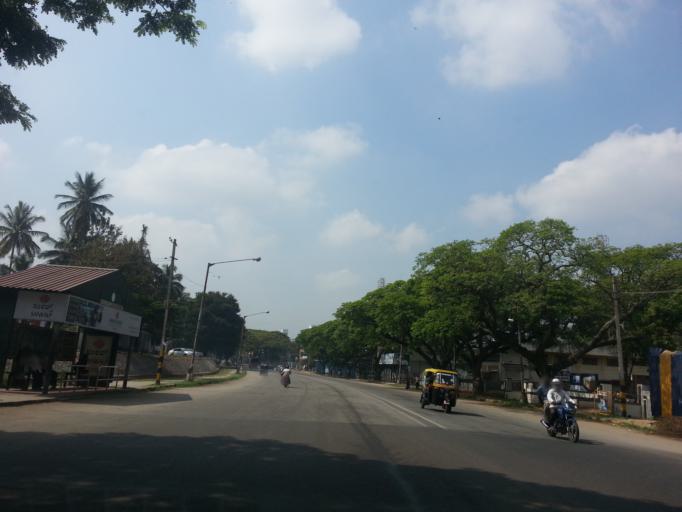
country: IN
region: Karnataka
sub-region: Mysore
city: Mysore
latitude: 12.3303
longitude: 76.6454
